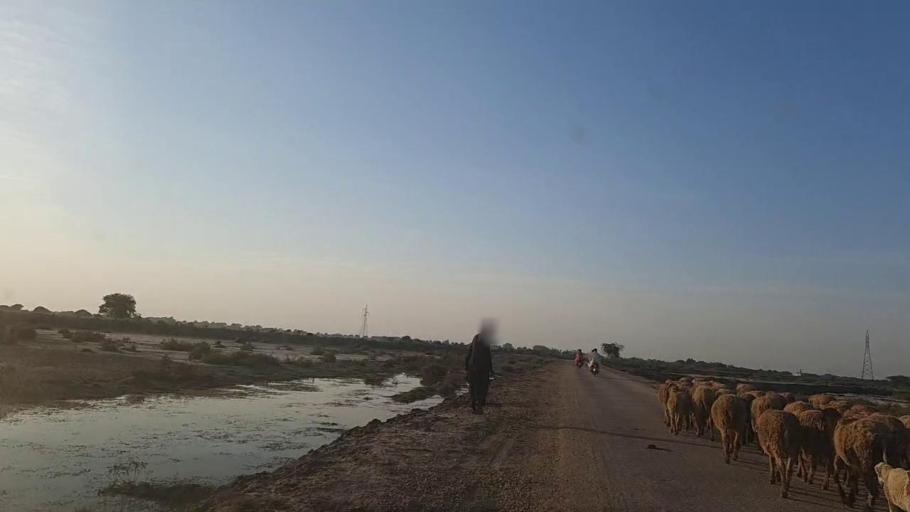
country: PK
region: Sindh
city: Mirpur Batoro
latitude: 24.6906
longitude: 68.2020
